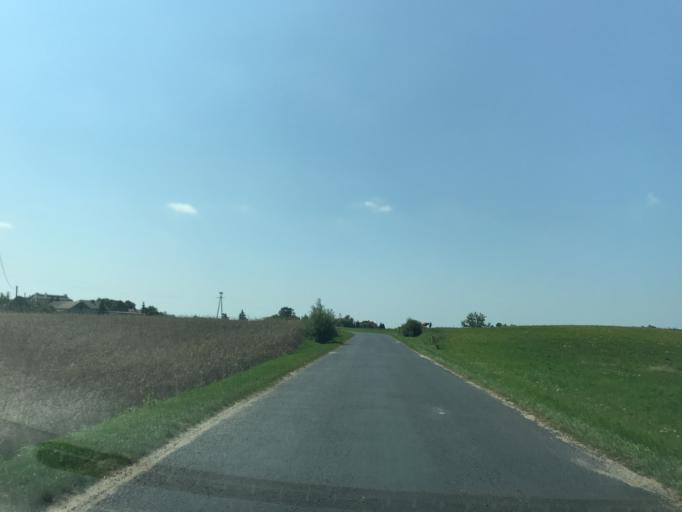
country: PL
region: Kujawsko-Pomorskie
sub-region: Powiat golubsko-dobrzynski
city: Zbojno
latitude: 52.9775
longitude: 19.2022
